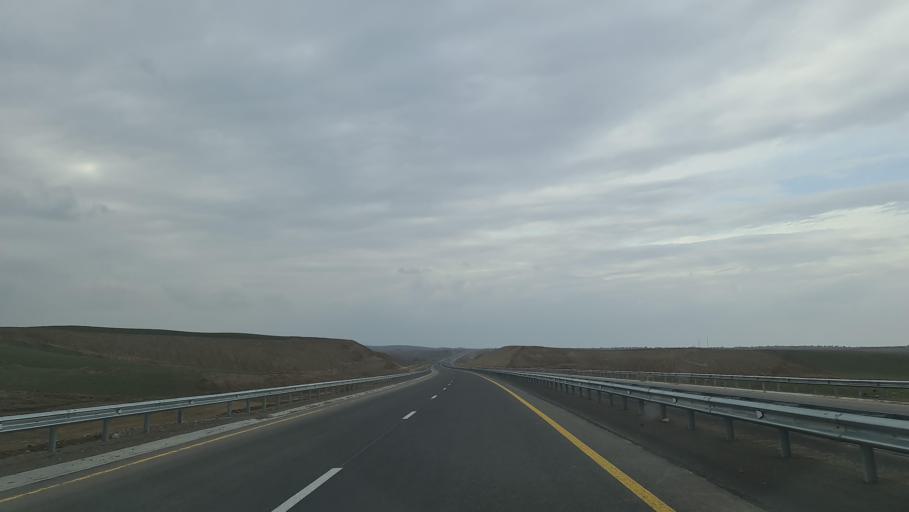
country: KZ
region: Almaty Oblysy
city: Burunday
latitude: 43.2972
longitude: 76.1726
